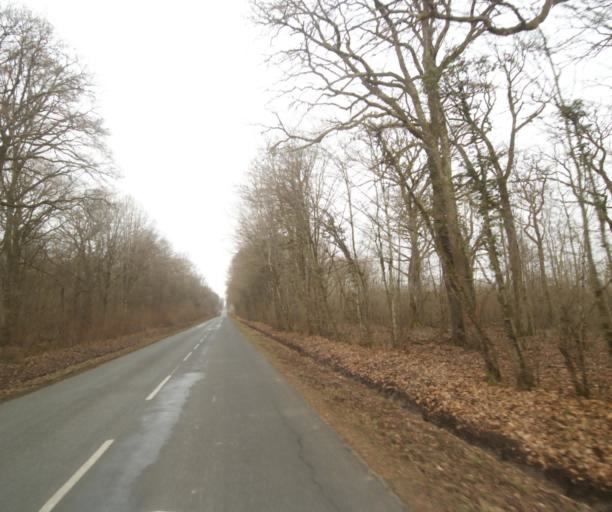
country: FR
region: Champagne-Ardenne
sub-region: Departement de la Haute-Marne
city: Villiers-en-Lieu
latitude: 48.7116
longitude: 4.8868
